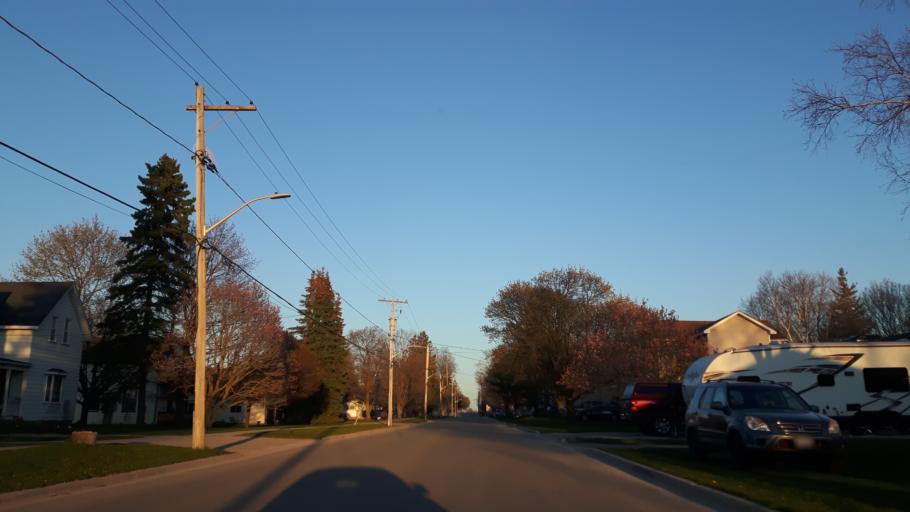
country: CA
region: Ontario
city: Bluewater
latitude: 43.6186
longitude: -81.5384
